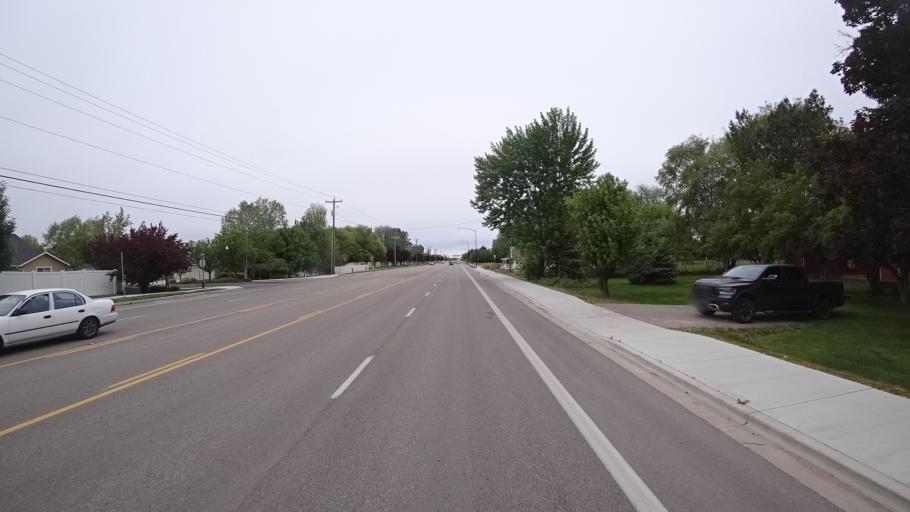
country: US
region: Idaho
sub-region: Ada County
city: Meridian
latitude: 43.6338
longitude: -116.3835
